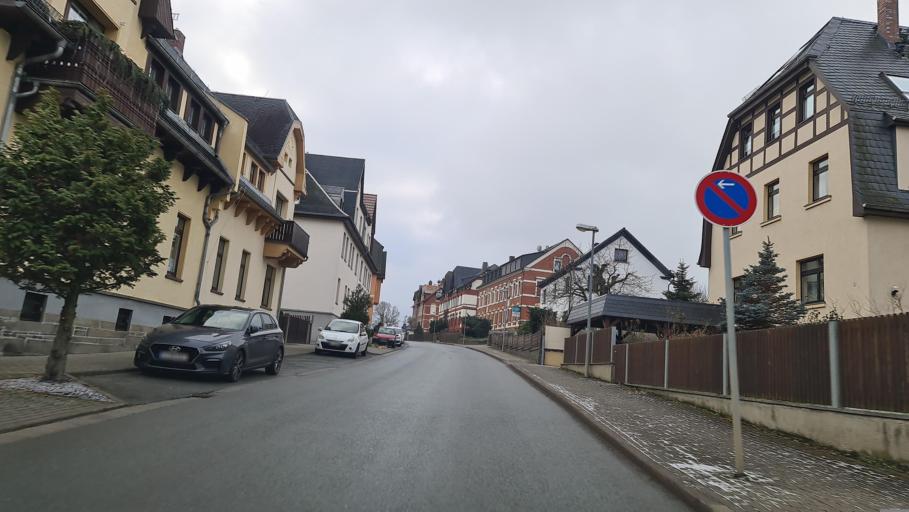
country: DE
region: Saxony
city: Weischlitz
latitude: 50.4509
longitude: 12.0582
